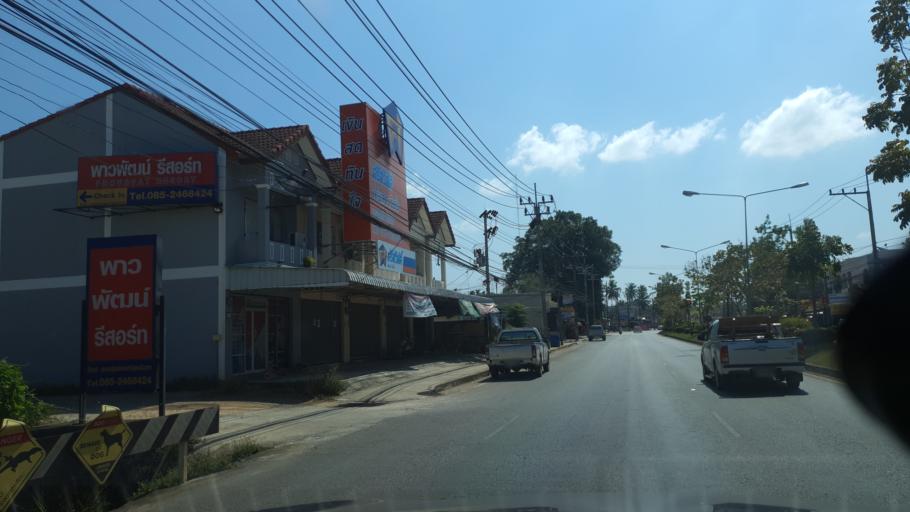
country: TH
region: Krabi
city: Krabi
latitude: 8.0779
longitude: 98.9036
